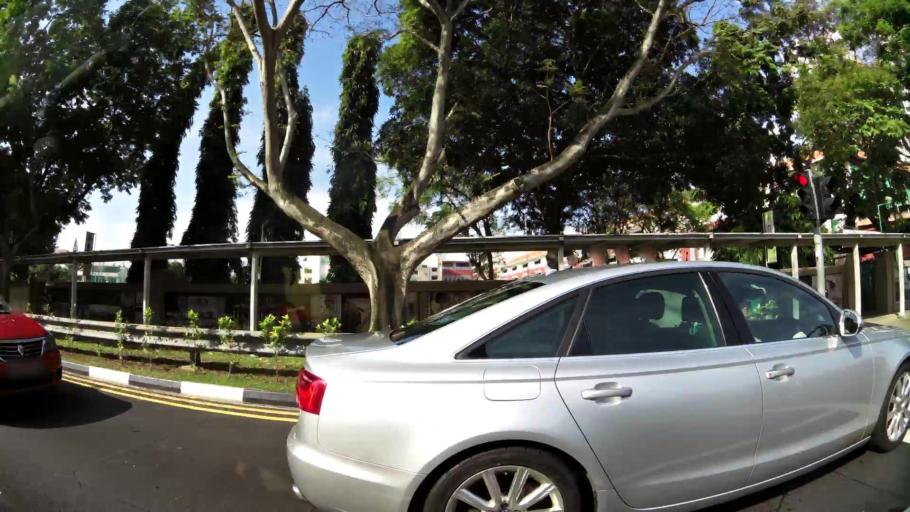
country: SG
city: Singapore
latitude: 1.3552
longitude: 103.8465
